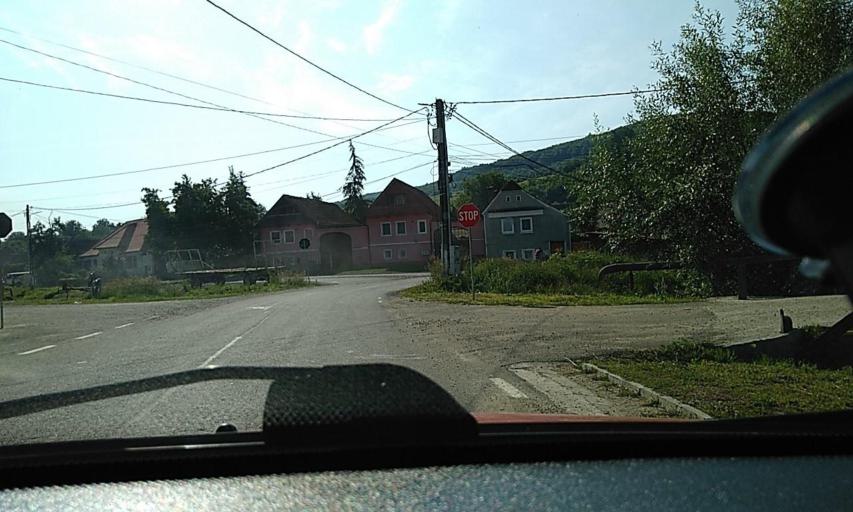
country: RO
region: Brasov
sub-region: Comuna Bunesti
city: Bunesti
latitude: 46.1048
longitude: 25.0585
